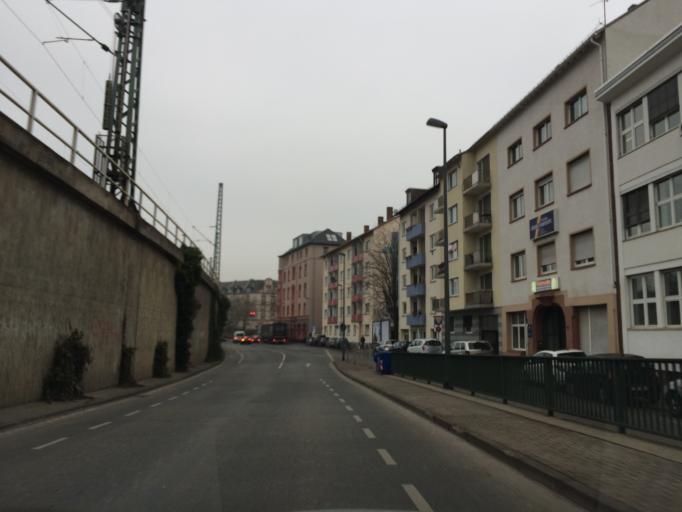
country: DE
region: Hesse
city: Niederrad
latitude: 50.1157
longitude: 8.6435
